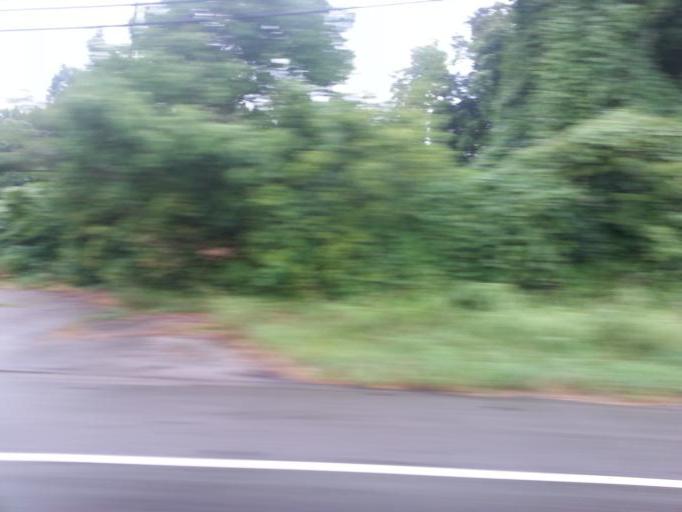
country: US
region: Tennessee
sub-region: Knox County
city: Knoxville
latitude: 35.9108
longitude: -83.8536
